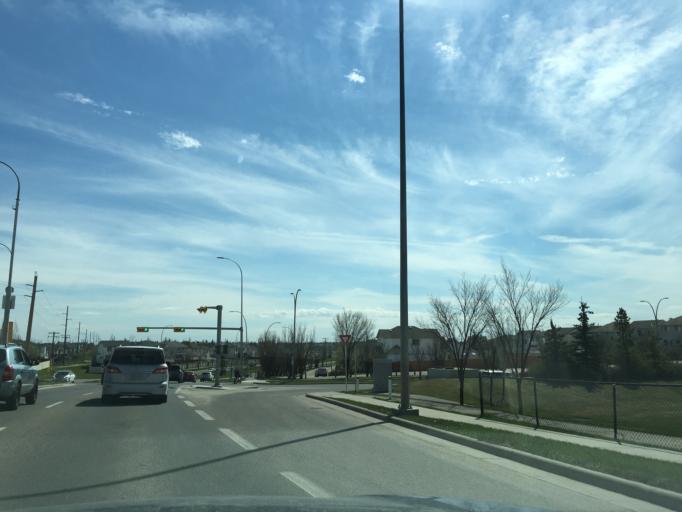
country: CA
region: Alberta
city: Calgary
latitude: 50.9067
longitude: -114.1063
